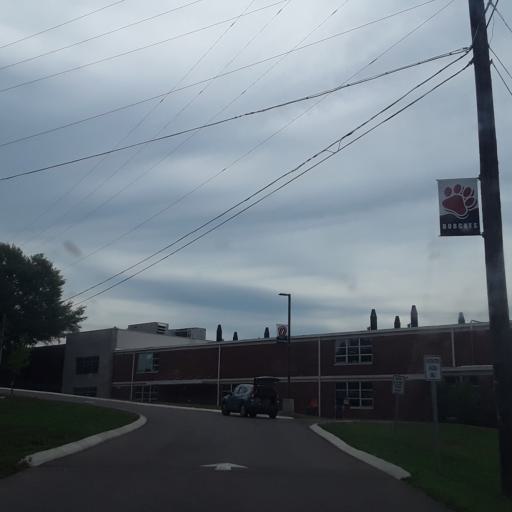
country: US
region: Tennessee
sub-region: Davidson County
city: Oak Hill
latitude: 36.0801
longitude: -86.7711
